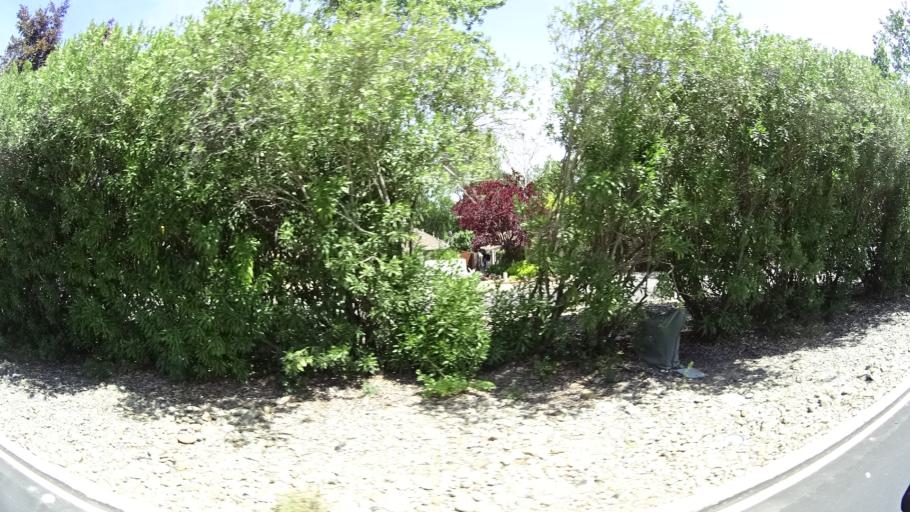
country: US
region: California
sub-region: Placer County
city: Rocklin
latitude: 38.7944
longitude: -121.2507
